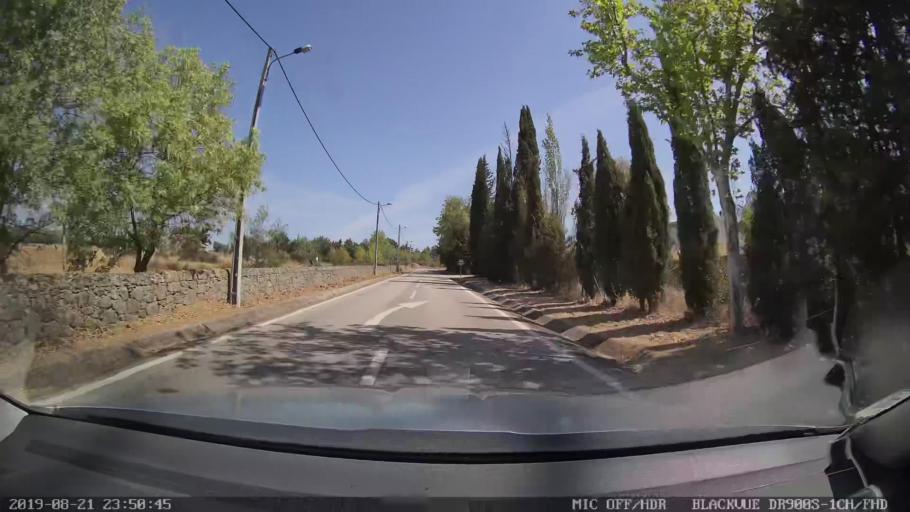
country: PT
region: Castelo Branco
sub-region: Idanha-A-Nova
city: Idanha-a-Nova
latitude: 39.8941
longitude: -7.2392
